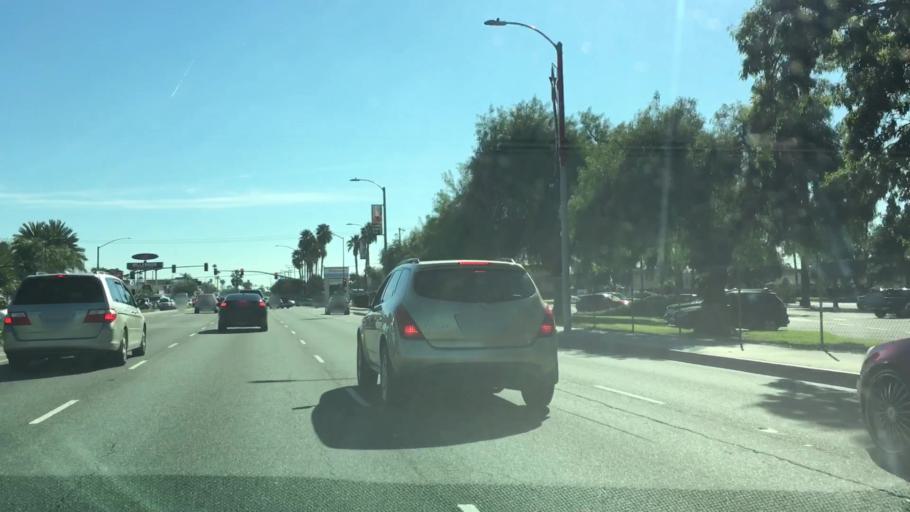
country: US
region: California
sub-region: Orange County
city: Buena Park
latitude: 33.8408
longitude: -117.9962
